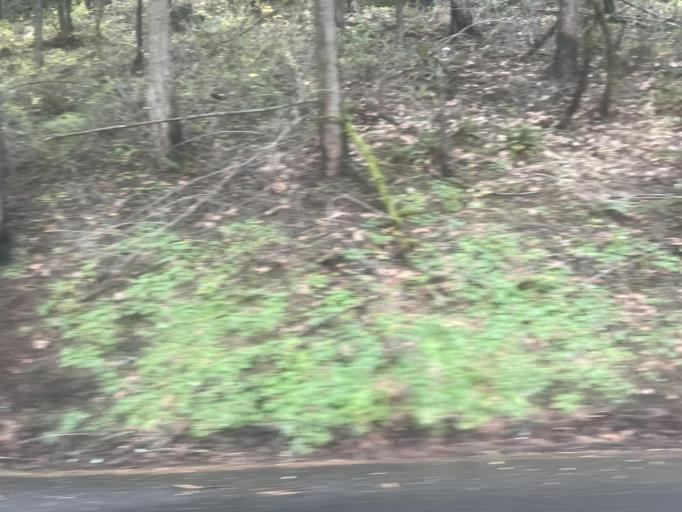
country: US
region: Washington
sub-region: Clark County
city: Washougal
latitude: 45.5446
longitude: -122.2005
